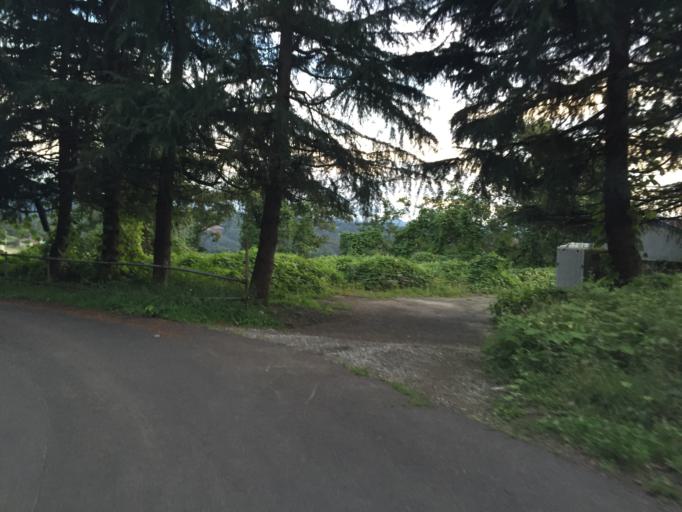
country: JP
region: Fukushima
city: Fukushima-shi
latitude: 37.7310
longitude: 140.4878
